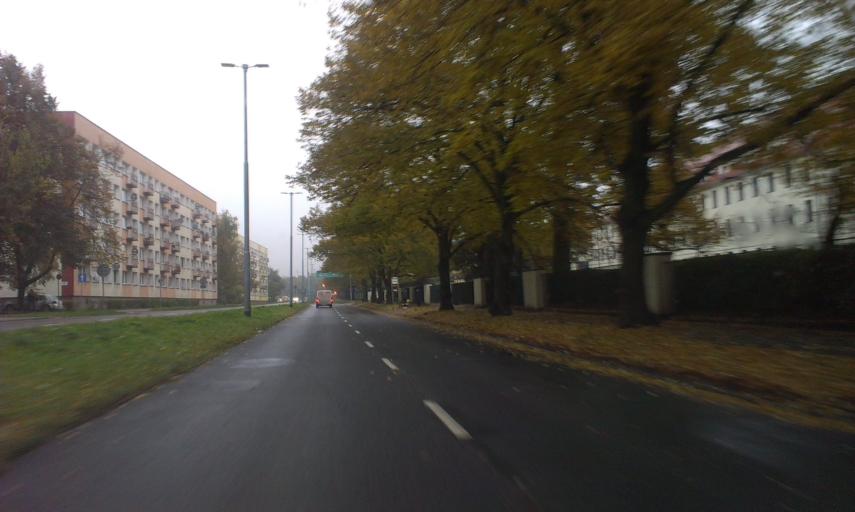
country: PL
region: West Pomeranian Voivodeship
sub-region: Koszalin
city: Koszalin
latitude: 54.1881
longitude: 16.2081
